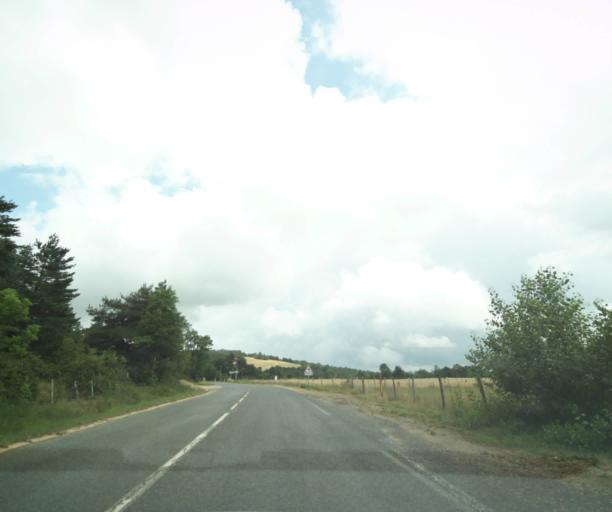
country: FR
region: Languedoc-Roussillon
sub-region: Departement de la Lozere
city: La Canourgue
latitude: 44.3978
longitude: 3.1402
